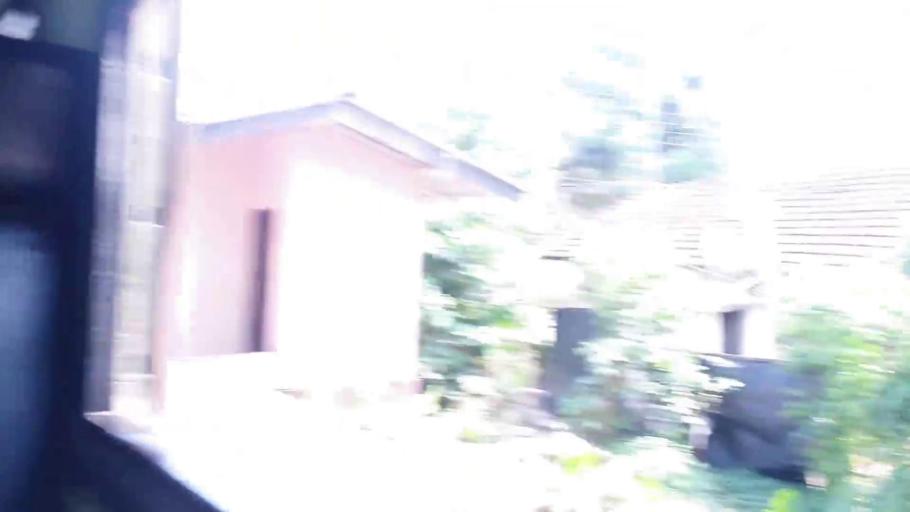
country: LK
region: Southern
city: Hikkaduwa
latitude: 6.1686
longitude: 80.0894
